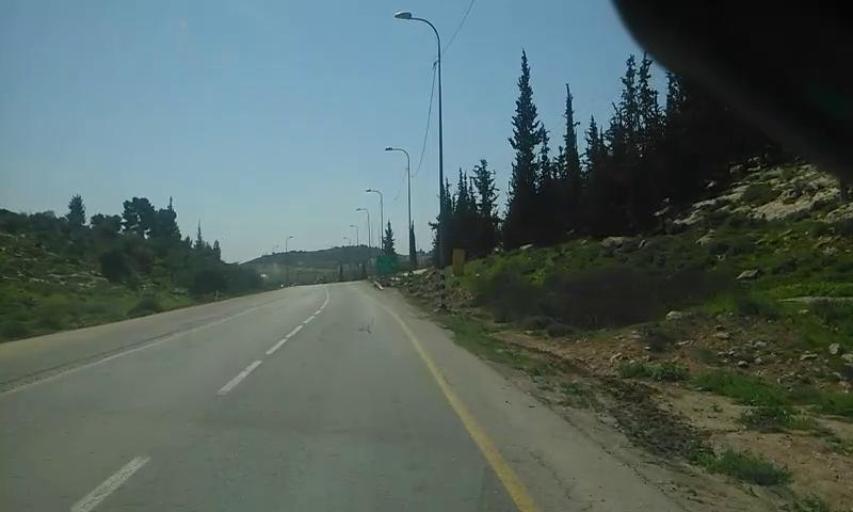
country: PS
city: Rabud
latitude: 31.4453
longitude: 35.0210
